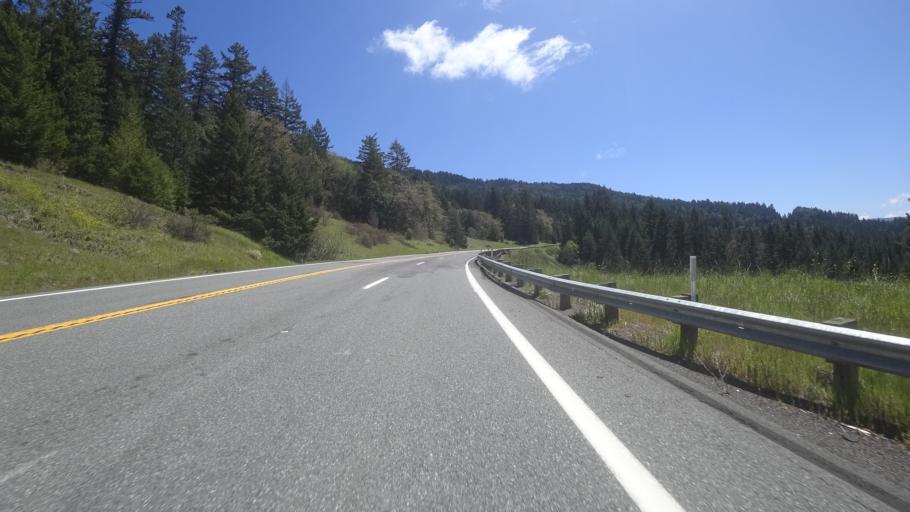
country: US
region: California
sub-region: Humboldt County
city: Willow Creek
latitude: 40.9258
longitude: -123.7921
